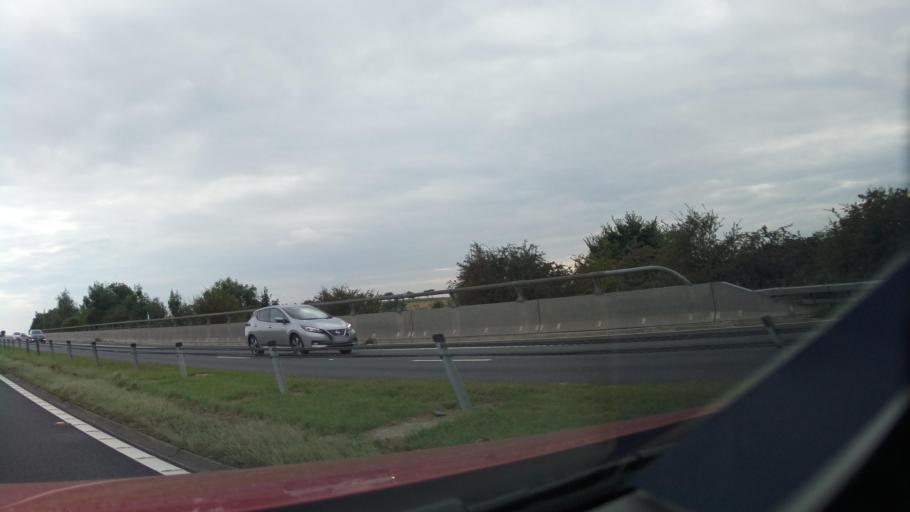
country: GB
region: England
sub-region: County Durham
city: Bishop Middleham
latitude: 54.6670
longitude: -1.4990
